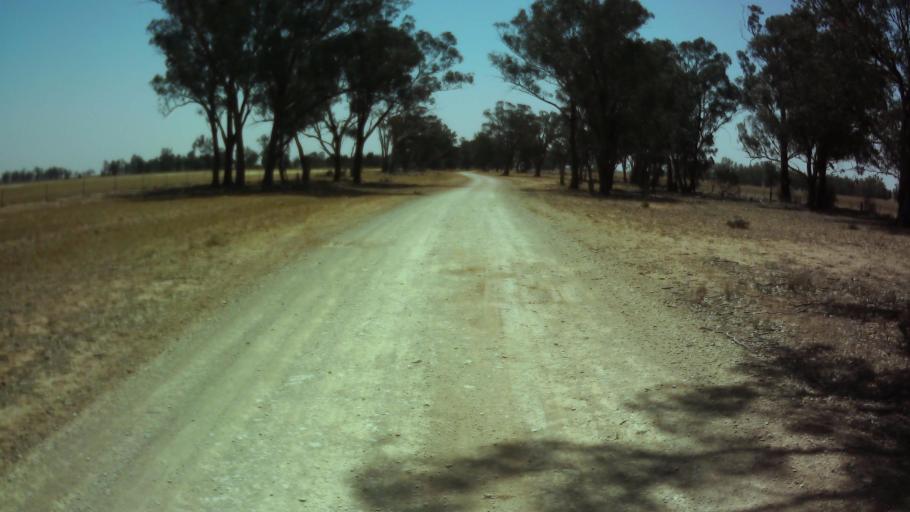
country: AU
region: New South Wales
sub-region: Weddin
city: Grenfell
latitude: -34.0194
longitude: 147.8999
